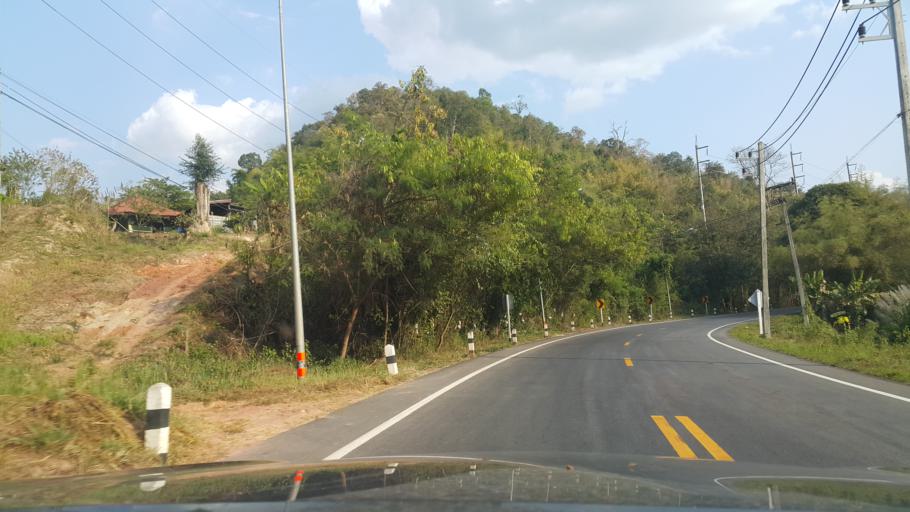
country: TH
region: Loei
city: Dan Sai
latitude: 17.2261
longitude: 101.0603
